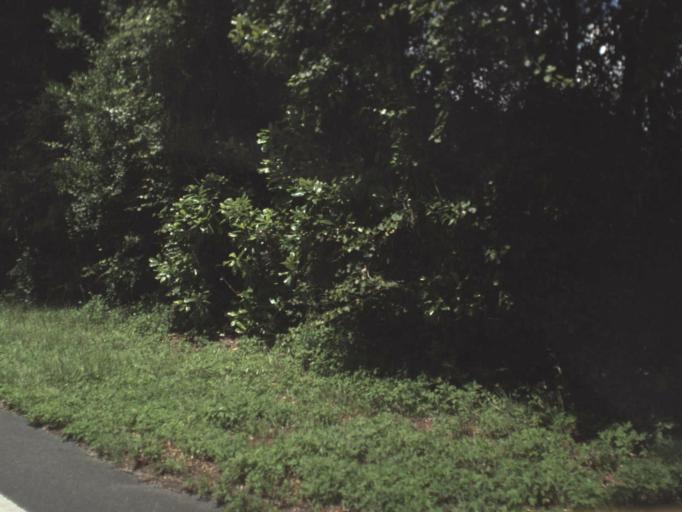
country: US
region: Florida
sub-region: Alachua County
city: Hawthorne
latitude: 29.6737
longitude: -82.0333
